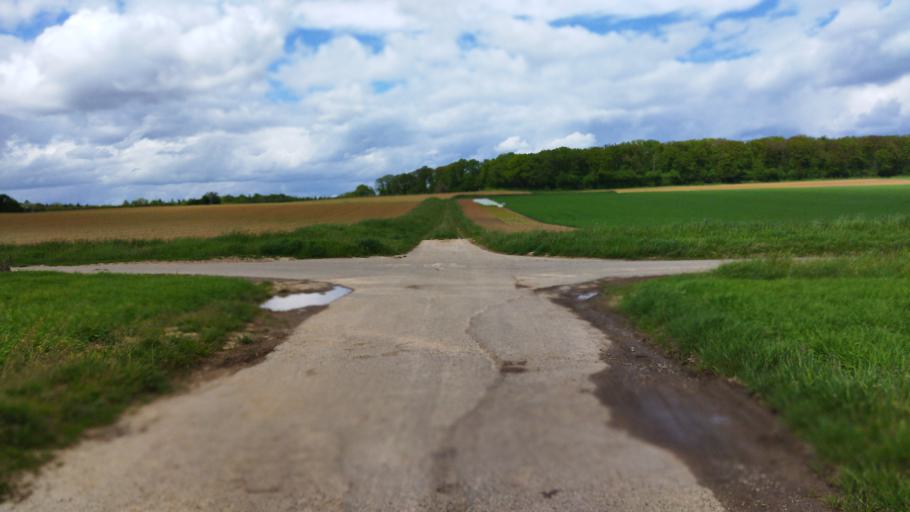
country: DE
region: Baden-Wuerttemberg
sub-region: Regierungsbezirk Stuttgart
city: Leingarten
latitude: 49.1940
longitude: 9.1224
